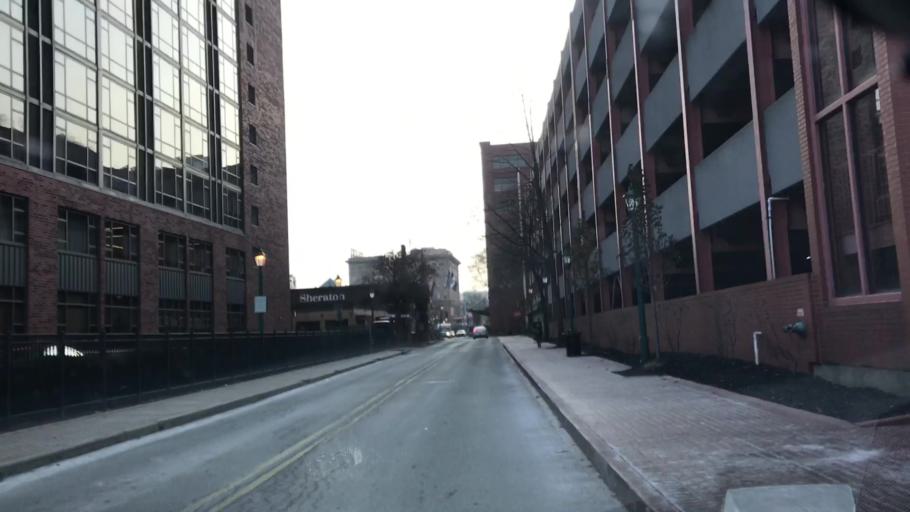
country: US
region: Pennsylvania
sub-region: Allegheny County
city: Pittsburgh
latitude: 40.4350
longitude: -80.0075
